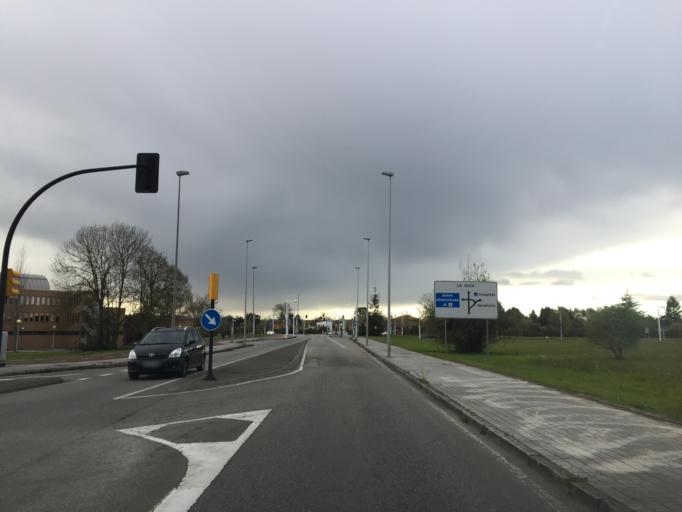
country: ES
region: Asturias
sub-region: Province of Asturias
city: Gijon
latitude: 43.5262
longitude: -5.6265
